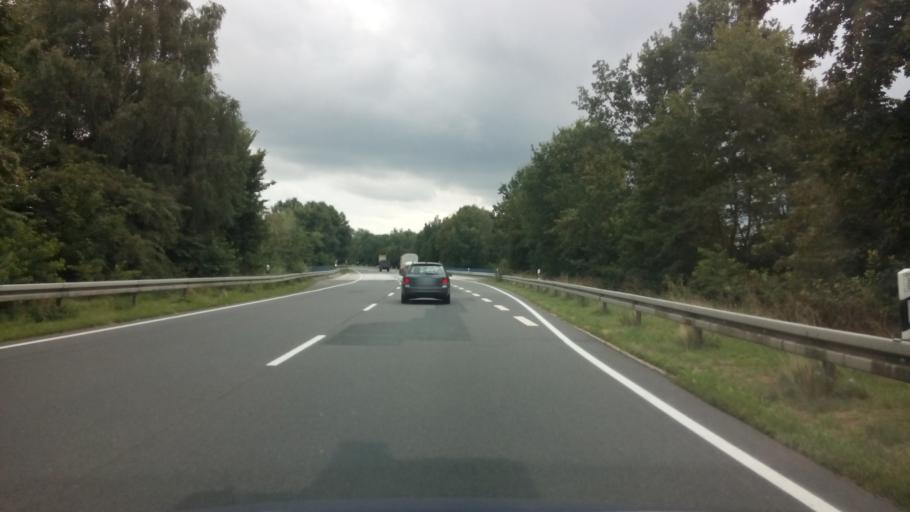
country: DE
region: Lower Saxony
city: Diepholz
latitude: 52.5970
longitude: 8.3535
